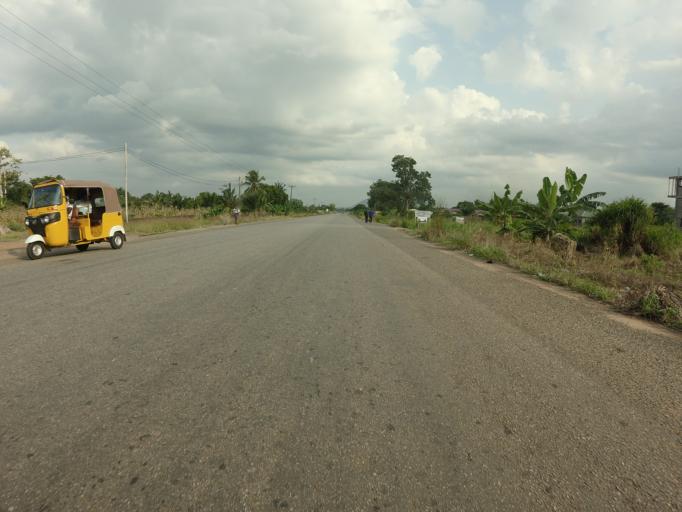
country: GH
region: Volta
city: Ho
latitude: 6.5826
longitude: 0.4809
